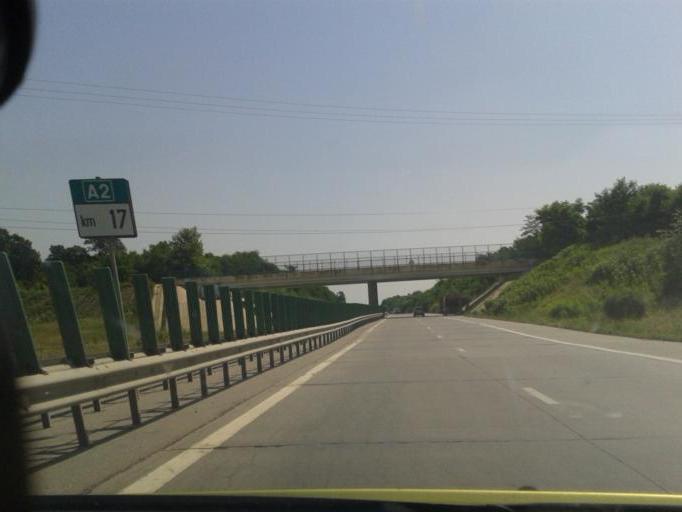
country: RO
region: Ilfov
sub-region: Comuna Cernica
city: Cernica
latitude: 44.4129
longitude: 26.2954
